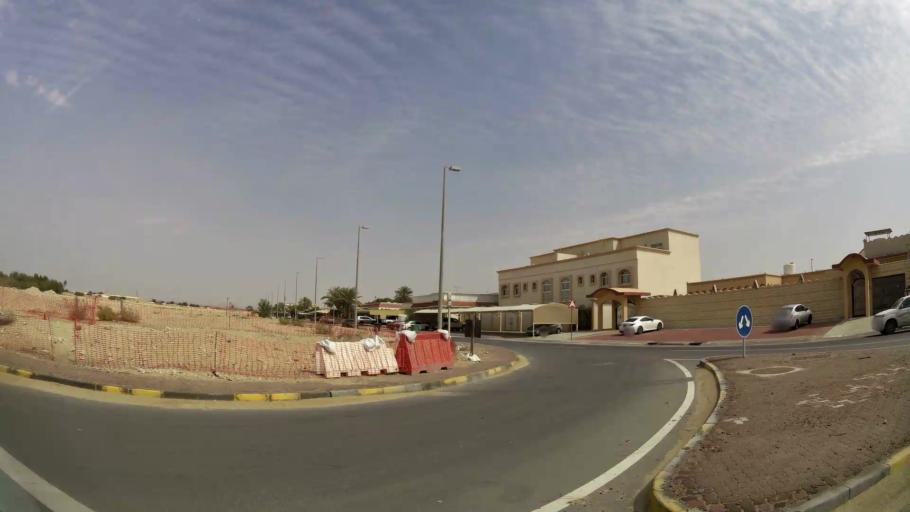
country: AE
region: Abu Dhabi
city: Abu Dhabi
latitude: 24.5585
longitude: 54.6783
